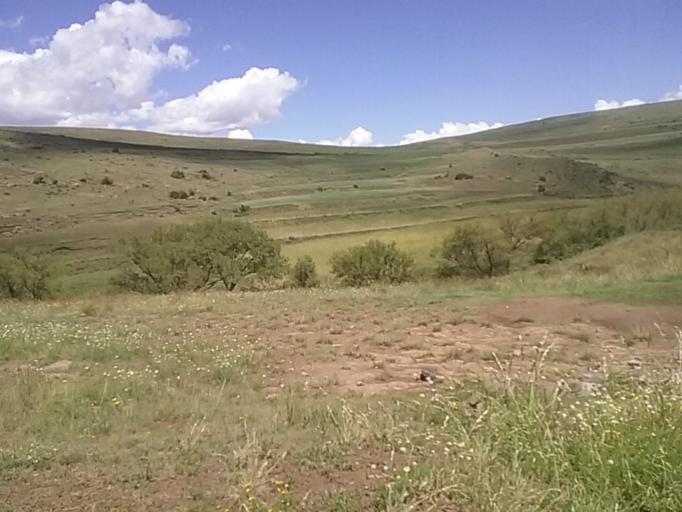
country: LS
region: Qacha's Nek
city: Qacha's Nek
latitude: -30.1651
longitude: 28.2210
